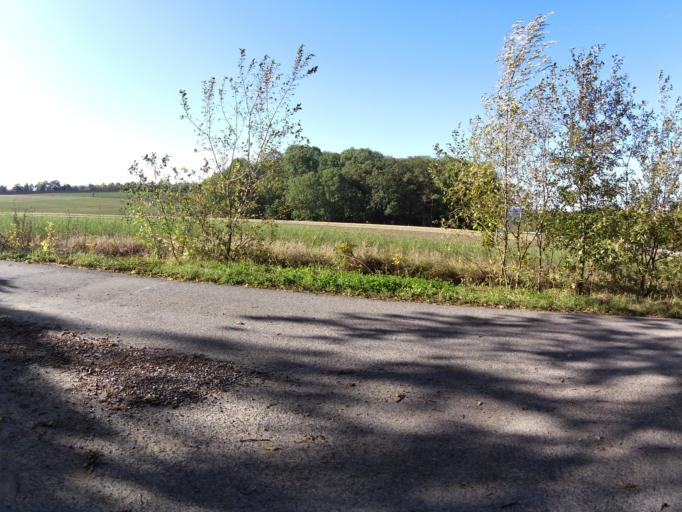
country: DE
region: Bavaria
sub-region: Regierungsbezirk Unterfranken
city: Theilheim
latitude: 49.7427
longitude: 10.0224
